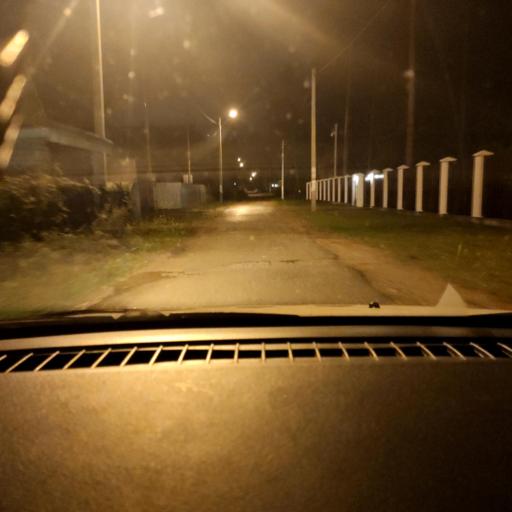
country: RU
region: Perm
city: Kondratovo
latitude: 58.0297
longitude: 55.9974
